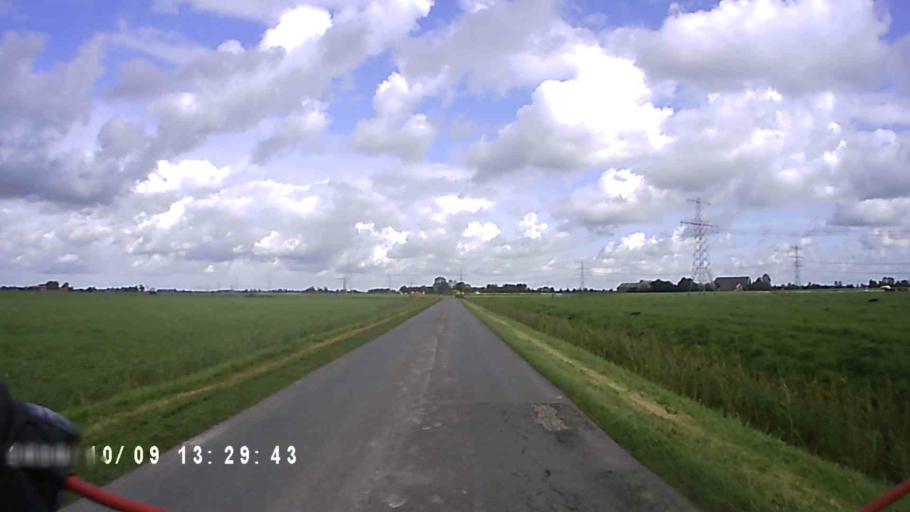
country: NL
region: Groningen
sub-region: Gemeente Zuidhorn
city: Aduard
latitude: 53.2731
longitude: 6.4718
